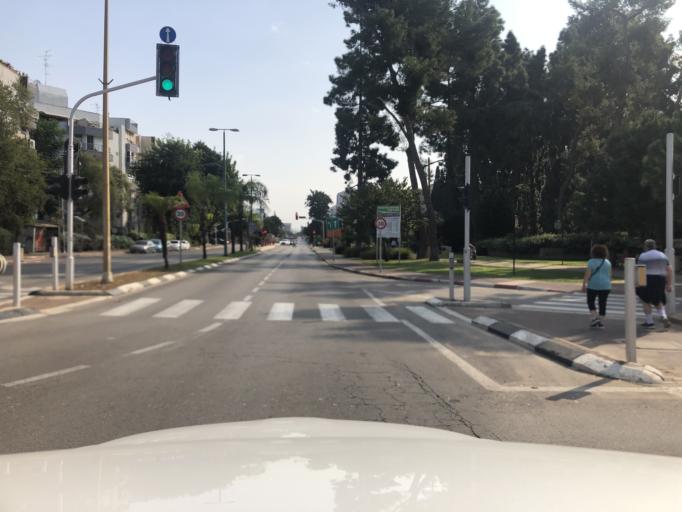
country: IL
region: Central District
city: Kfar Saba
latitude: 32.1737
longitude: 34.9154
